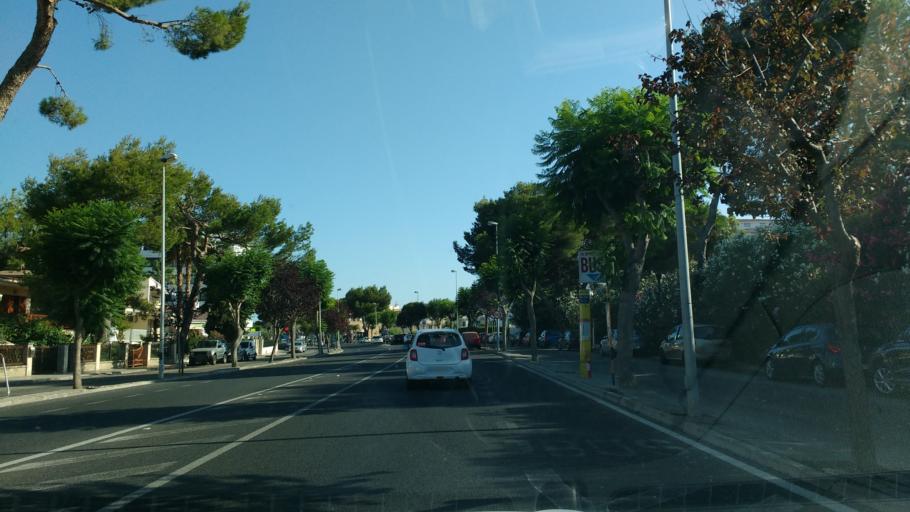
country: ES
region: Balearic Islands
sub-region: Illes Balears
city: Port d'Alcudia
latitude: 39.8177
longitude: 3.1139
